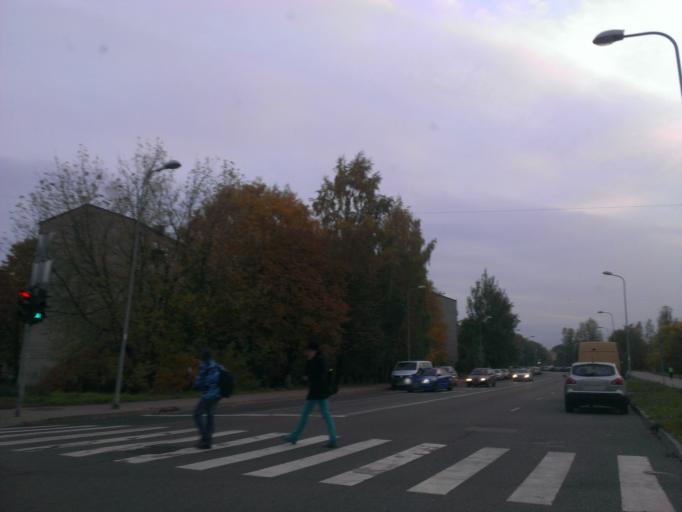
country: LV
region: Riga
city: Riga
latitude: 56.9727
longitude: 24.1297
